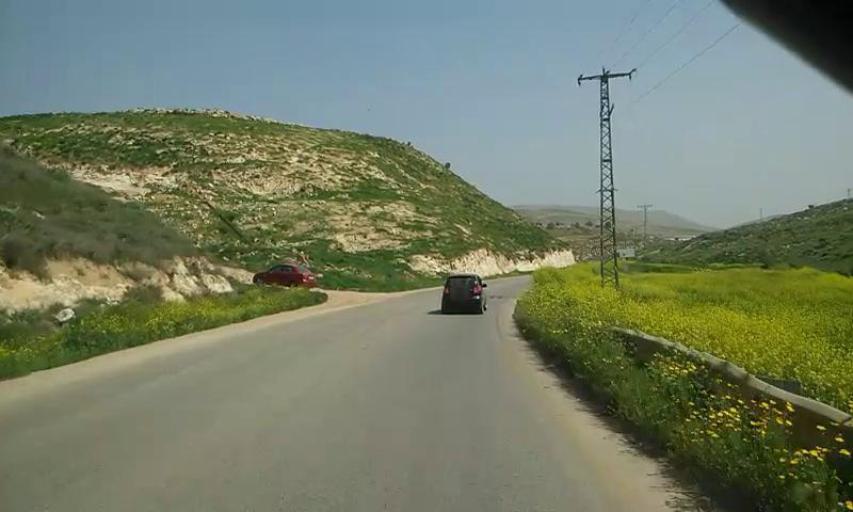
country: PS
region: West Bank
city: Tubas
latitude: 32.2973
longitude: 35.3602
